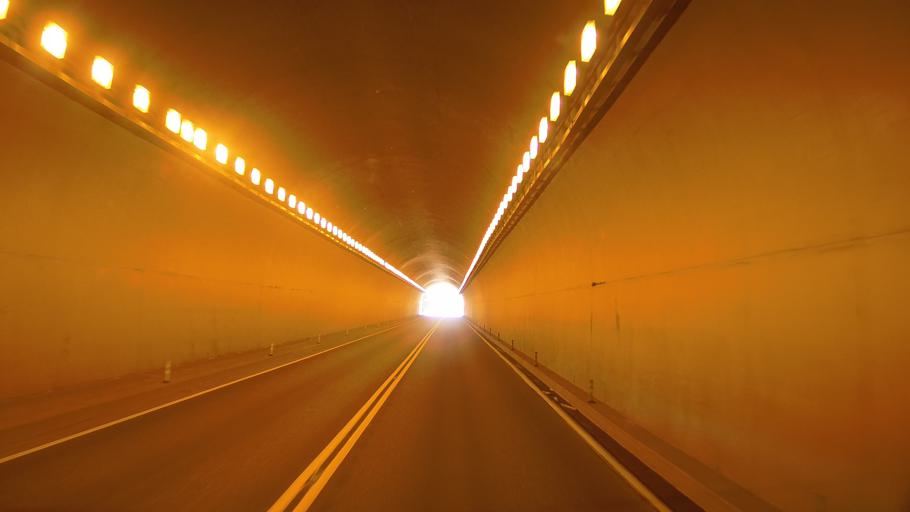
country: CA
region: British Columbia
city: Hope
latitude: 49.6268
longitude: -121.3939
